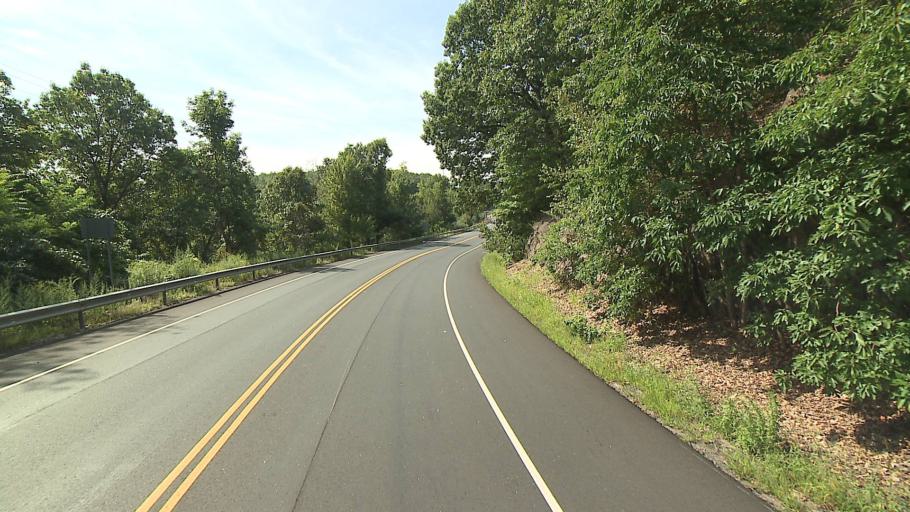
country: US
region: Connecticut
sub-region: Litchfield County
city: Oakville
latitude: 41.6077
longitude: -73.0617
